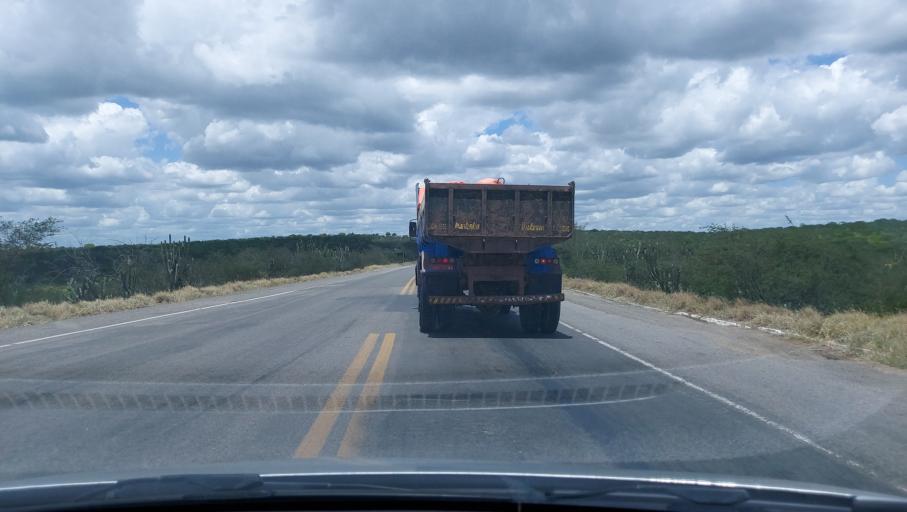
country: BR
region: Bahia
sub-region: Castro Alves
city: Castro Alves
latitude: -12.5822
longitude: -39.5223
